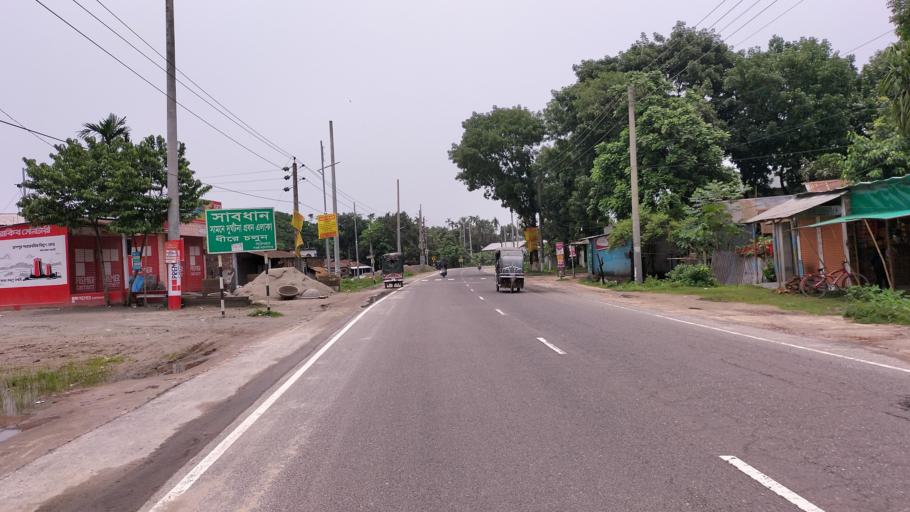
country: BD
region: Dhaka
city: Mymensingh
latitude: 24.7723
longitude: 90.4573
